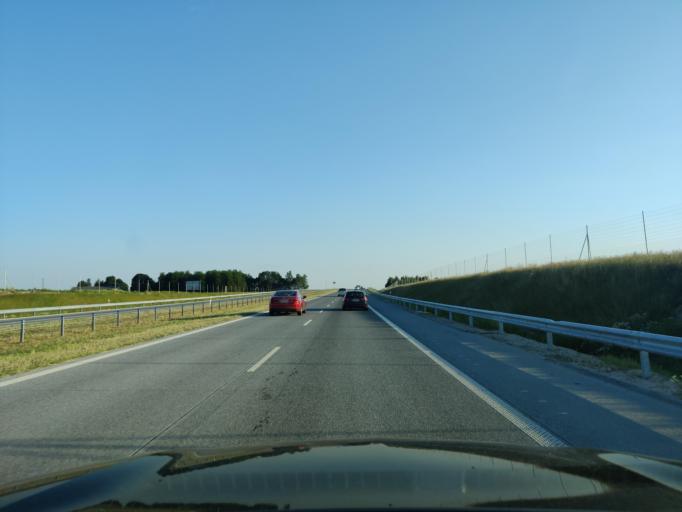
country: PL
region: Masovian Voivodeship
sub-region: Powiat mlawski
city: Wisniewo
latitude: 53.0390
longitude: 20.3566
